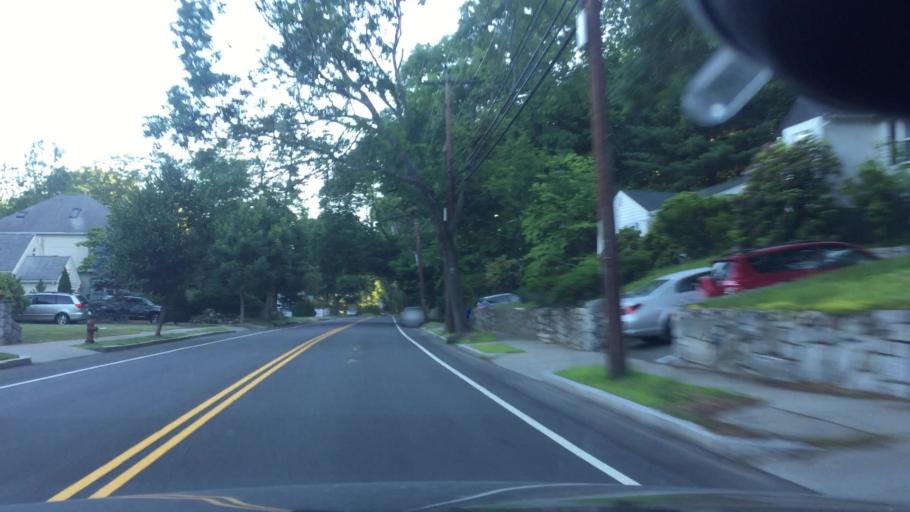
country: US
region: Massachusetts
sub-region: Middlesex County
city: Newton
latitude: 42.3101
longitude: -71.2080
